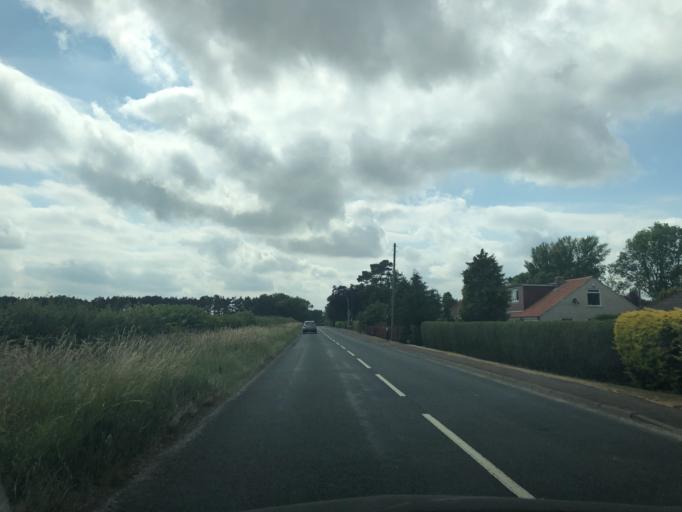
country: GB
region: England
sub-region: North Yorkshire
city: Stokesley
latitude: 54.4657
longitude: -1.2162
